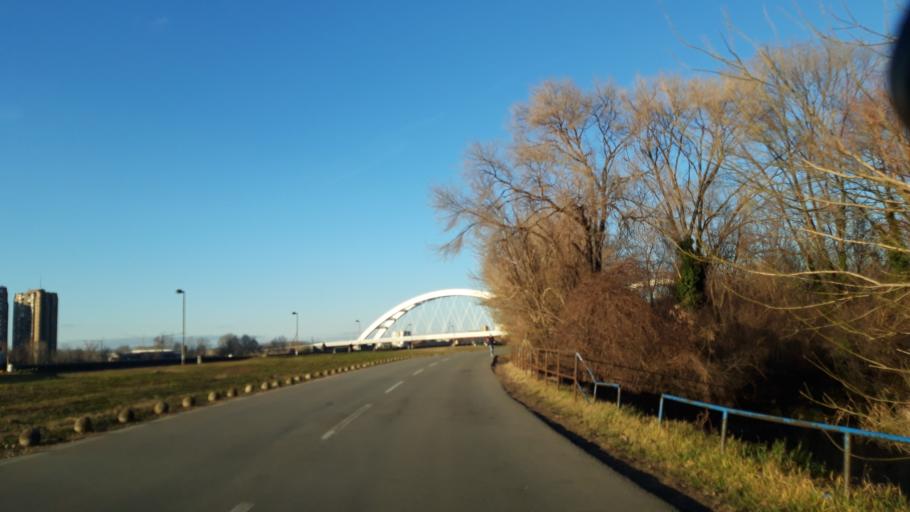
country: RS
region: Autonomna Pokrajina Vojvodina
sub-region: Juznobacki Okrug
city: Petrovaradin
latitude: 45.2567
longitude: 19.8591
